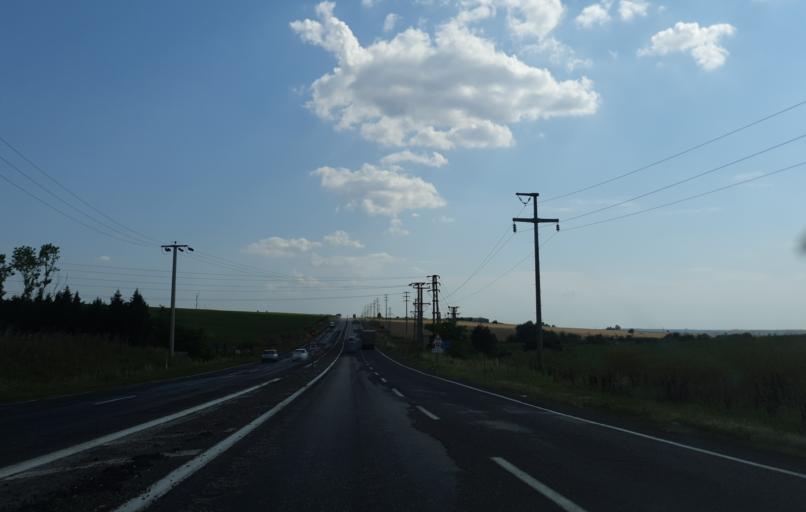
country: TR
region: Kirklareli
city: Buyukkaristiran
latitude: 41.2622
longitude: 27.5478
